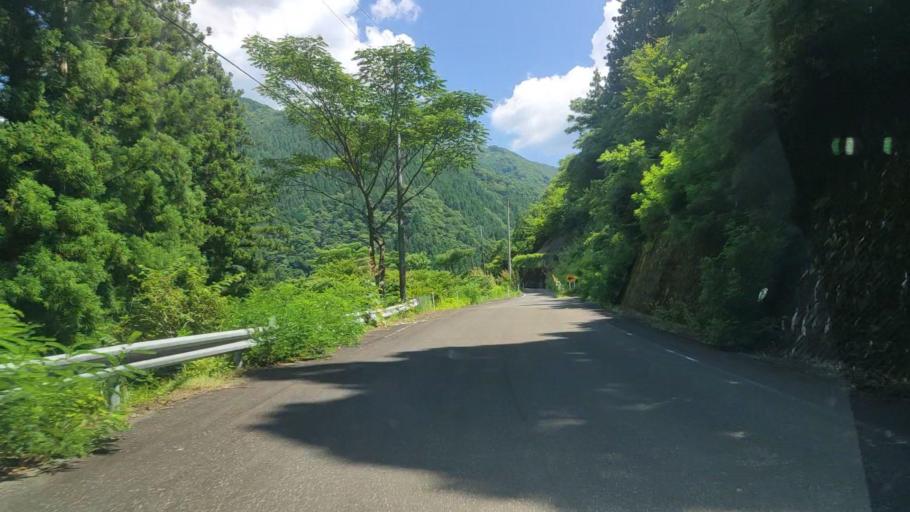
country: JP
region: Fukui
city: Ono
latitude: 35.7215
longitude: 136.5815
